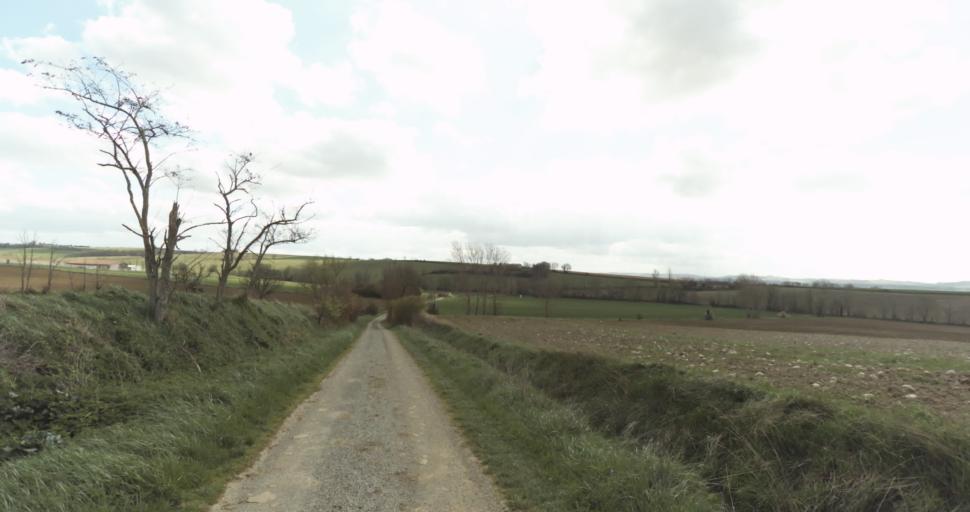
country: FR
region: Midi-Pyrenees
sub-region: Departement de la Haute-Garonne
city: Auterive
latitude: 43.3881
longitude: 1.4718
